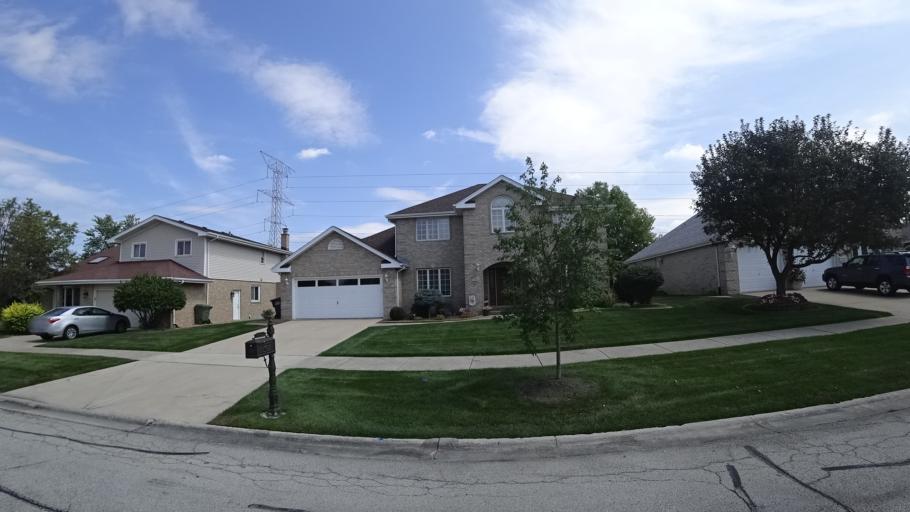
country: US
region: Illinois
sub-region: Cook County
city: Orland Hills
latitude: 41.5710
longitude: -87.8189
